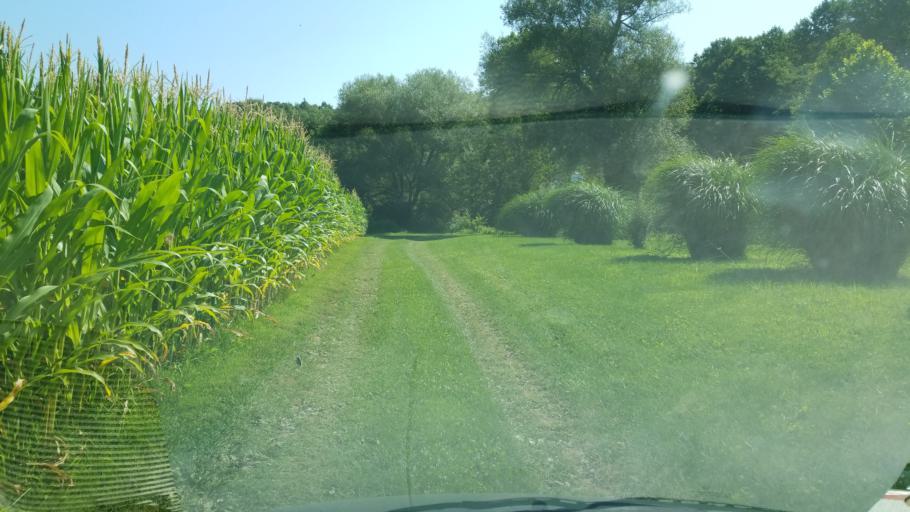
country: US
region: Ohio
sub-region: Richland County
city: Mansfield
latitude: 40.7179
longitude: -82.4954
